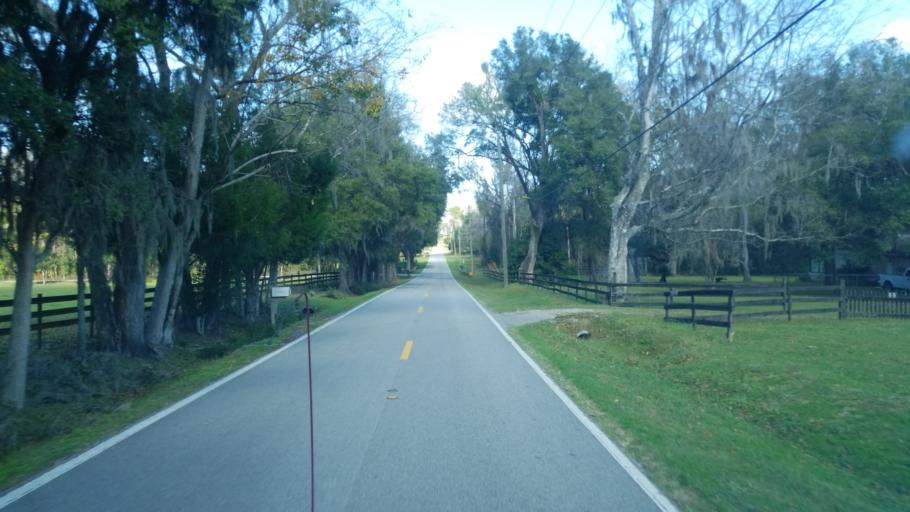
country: US
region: Florida
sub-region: Hernando County
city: North Brooksville
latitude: 28.6118
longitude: -82.3801
